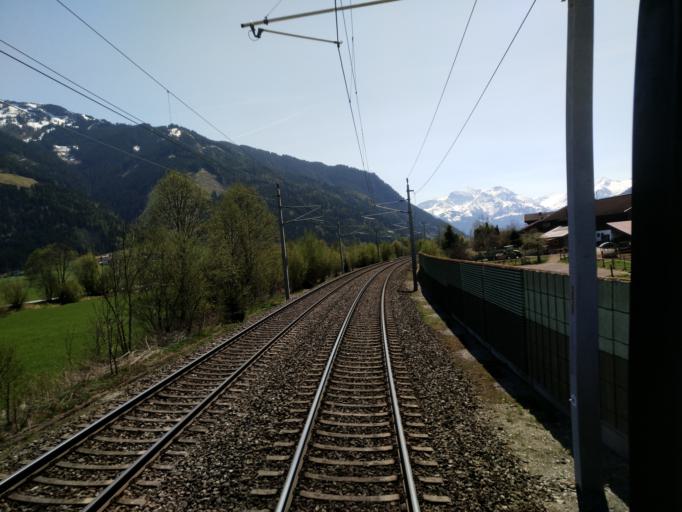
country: AT
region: Salzburg
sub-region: Politischer Bezirk Zell am See
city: Saalfelden am Steinernen Meer
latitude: 47.3953
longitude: 12.8308
